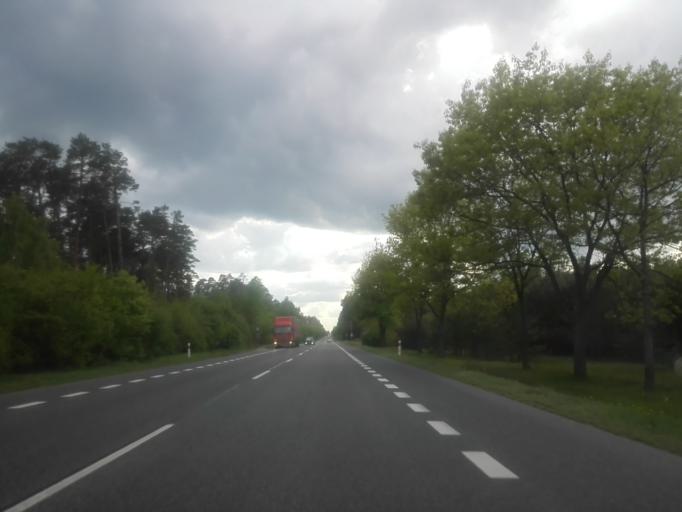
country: PL
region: Masovian Voivodeship
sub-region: Powiat ostrowski
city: Ostrow Mazowiecka
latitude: 52.8419
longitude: 21.9654
